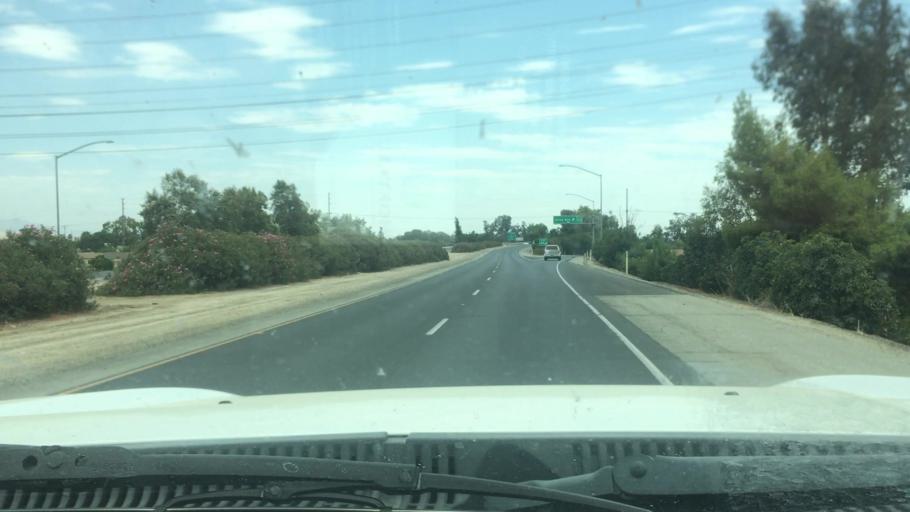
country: US
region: California
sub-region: Tulare County
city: Porterville
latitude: 36.0701
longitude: -119.0398
